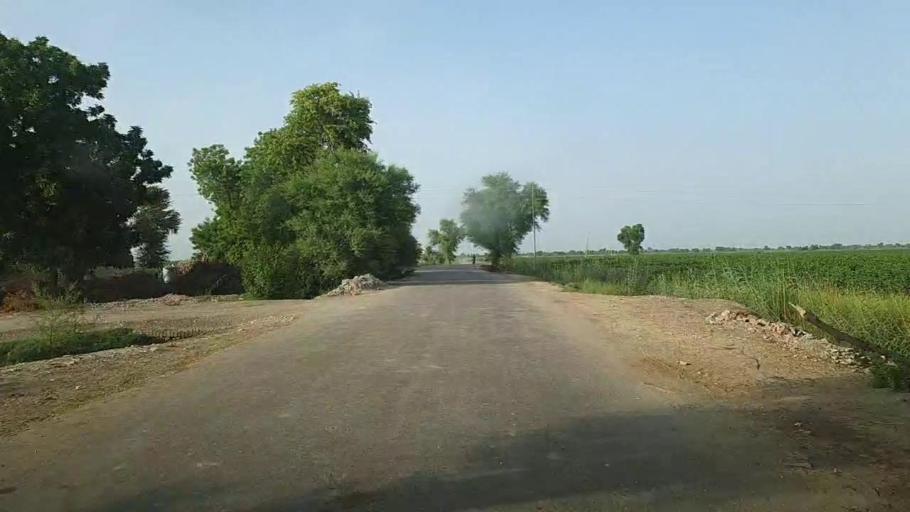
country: PK
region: Sindh
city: Khairpur
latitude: 28.0872
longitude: 69.8015
